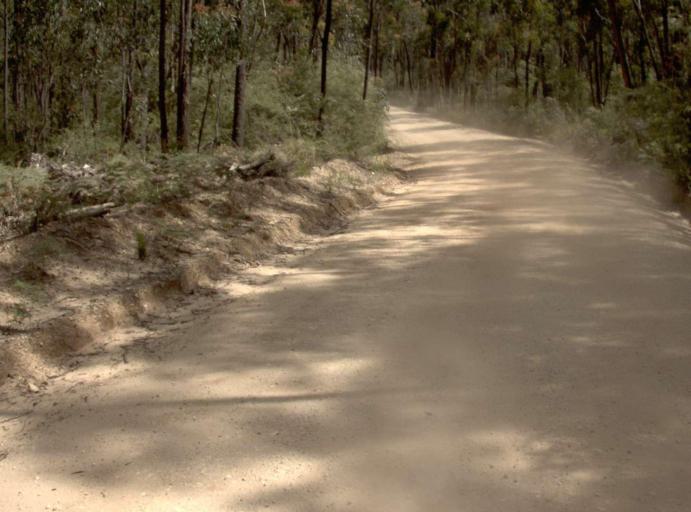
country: AU
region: Victoria
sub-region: East Gippsland
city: Lakes Entrance
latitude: -37.6656
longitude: 148.6331
